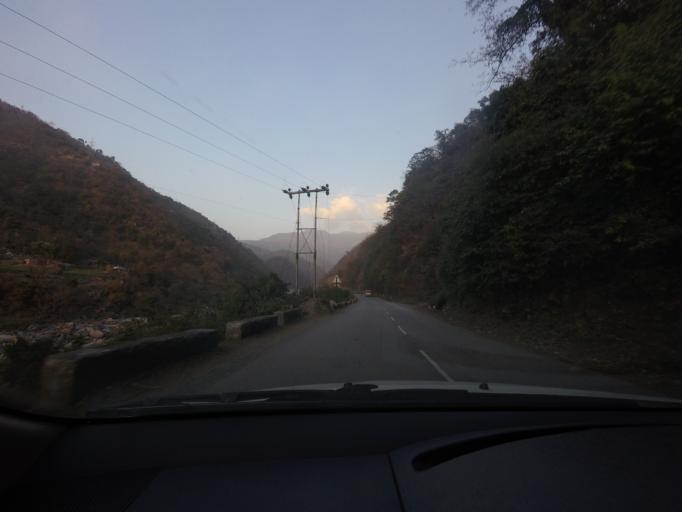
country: IN
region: Himachal Pradesh
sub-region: Mandi
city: Mandi
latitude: 31.7091
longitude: 76.9886
